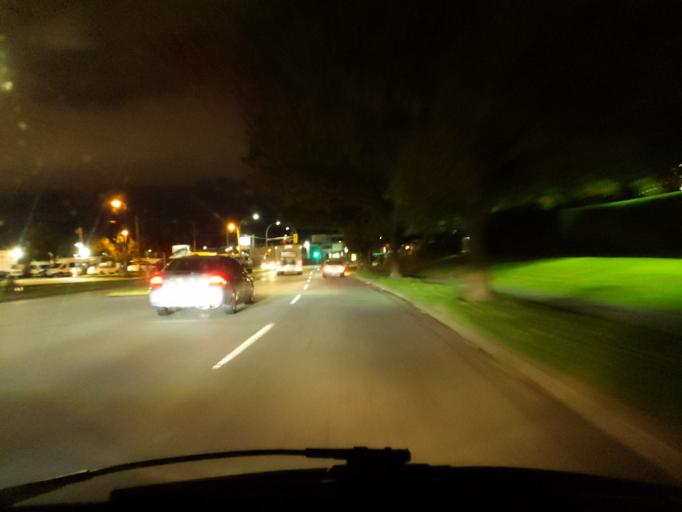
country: CA
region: British Columbia
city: Burnaby
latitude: 49.2602
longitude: -123.0132
